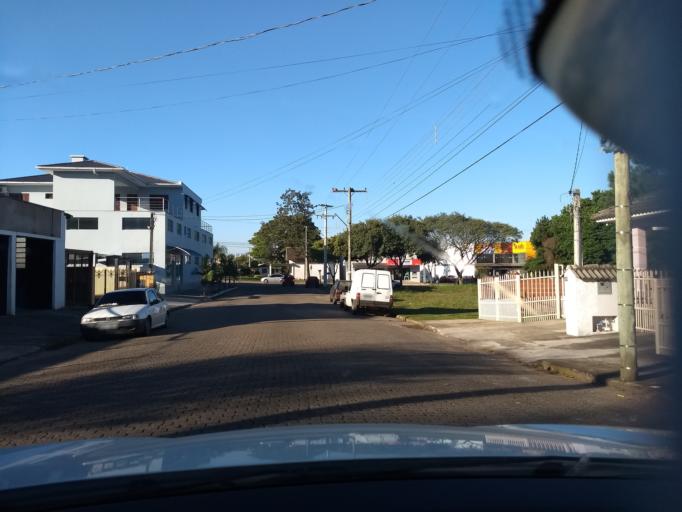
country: BR
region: Rio Grande do Sul
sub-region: Santa Cruz Do Sul
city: Santa Cruz do Sul
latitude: -29.7146
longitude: -52.5069
